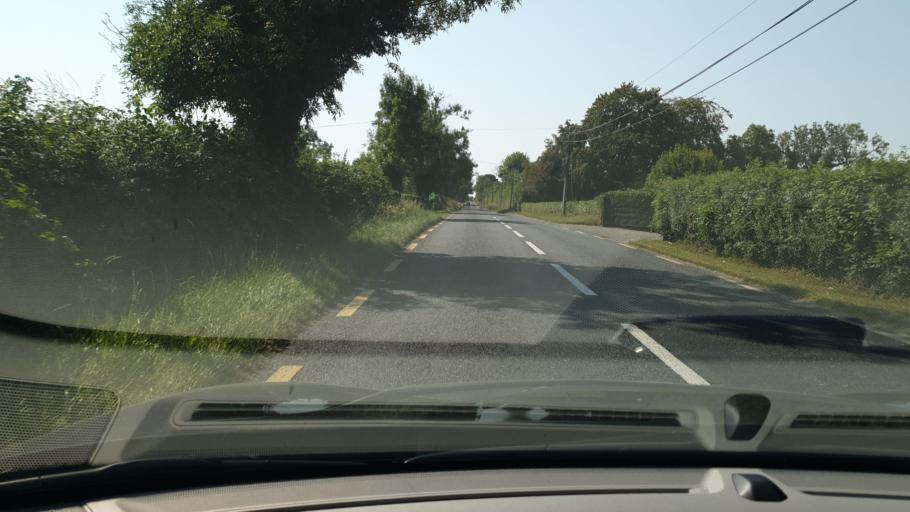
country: IE
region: Leinster
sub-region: Kildare
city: Kilcock
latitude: 53.4776
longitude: -6.7026
